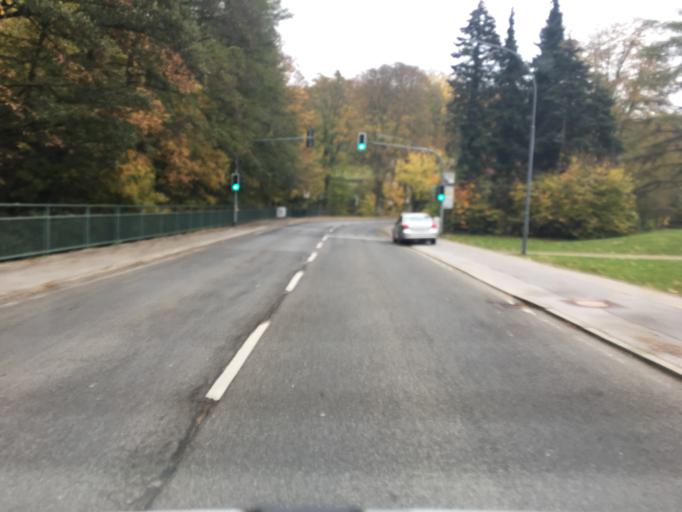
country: DE
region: North Rhine-Westphalia
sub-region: Regierungsbezirk Dusseldorf
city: Velbert
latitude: 51.3178
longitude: 7.0856
